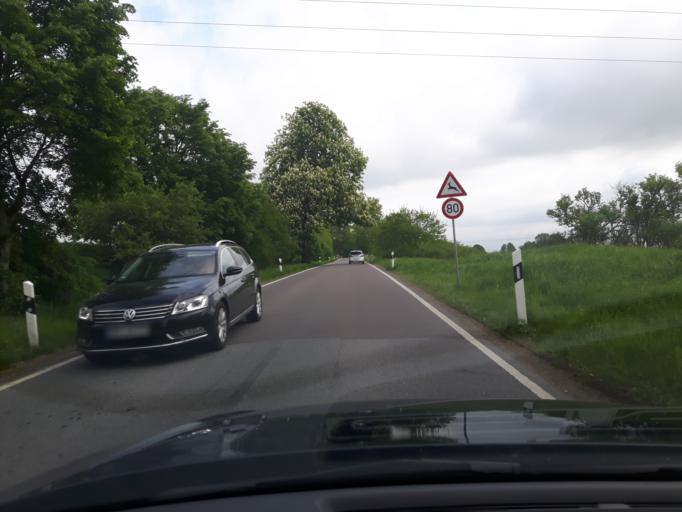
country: DE
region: Mecklenburg-Vorpommern
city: Gross Wokern
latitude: 53.6542
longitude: 12.4982
